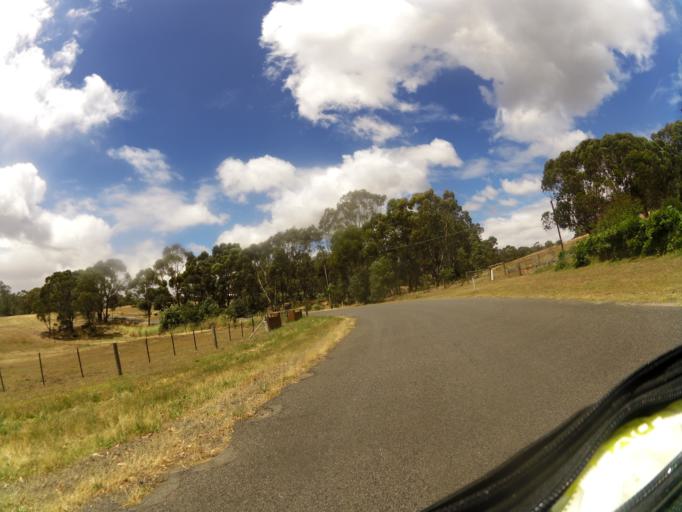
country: AU
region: Victoria
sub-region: Mount Alexander
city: Castlemaine
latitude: -37.0214
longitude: 144.2475
